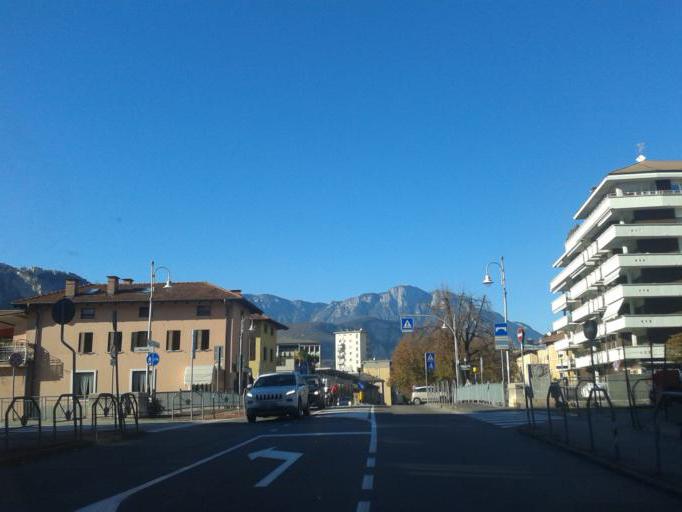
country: IT
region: Trentino-Alto Adige
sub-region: Provincia di Trento
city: Trento
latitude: 46.0585
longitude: 11.1274
